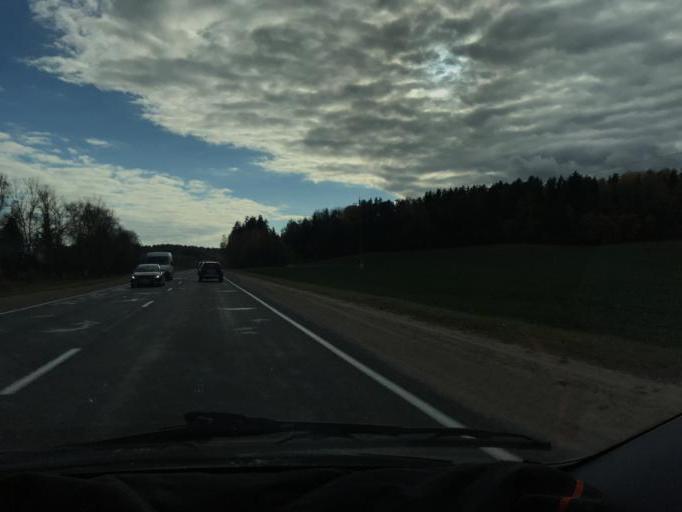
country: BY
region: Minsk
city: Lahoysk
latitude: 54.2266
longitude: 27.8341
